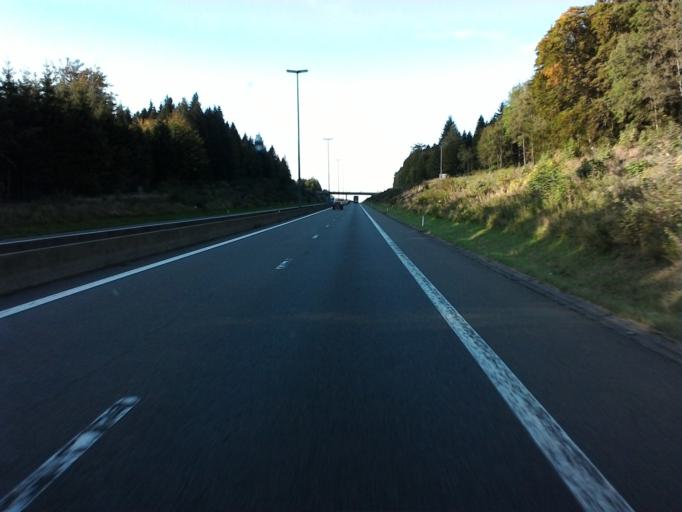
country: BE
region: Wallonia
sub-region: Province de Liege
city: Lierneux
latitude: 50.2128
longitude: 5.7753
